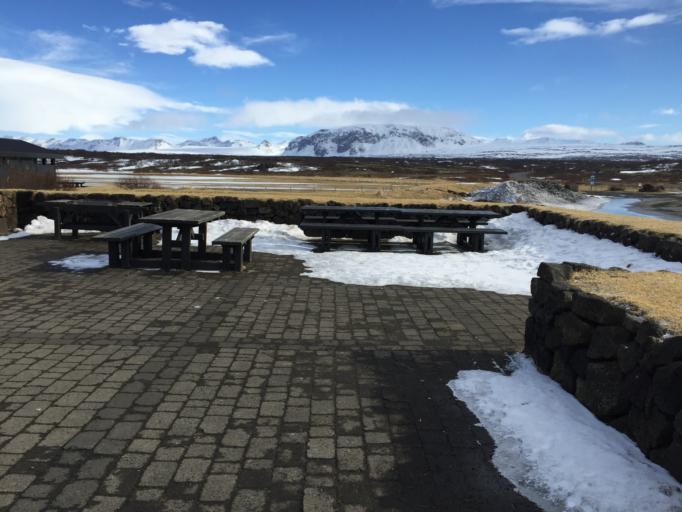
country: IS
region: South
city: Hveragerdi
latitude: 64.2797
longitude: -21.0880
